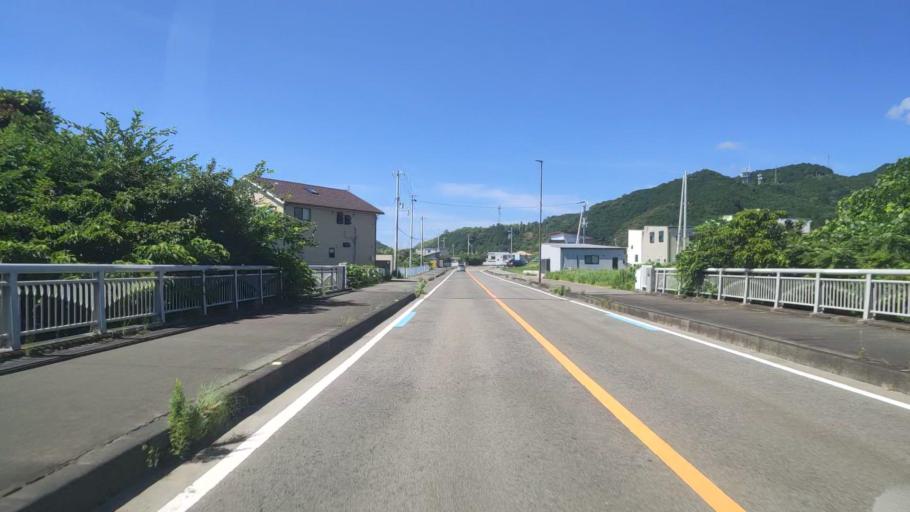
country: JP
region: Wakayama
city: Shingu
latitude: 33.7069
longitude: 135.9943
